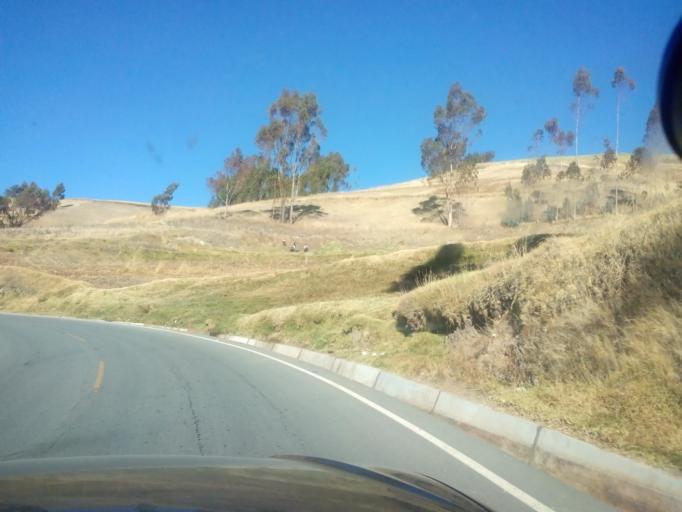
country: PE
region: Apurimac
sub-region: Provincia de Andahuaylas
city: Pacucha
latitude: -13.6564
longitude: -73.2931
